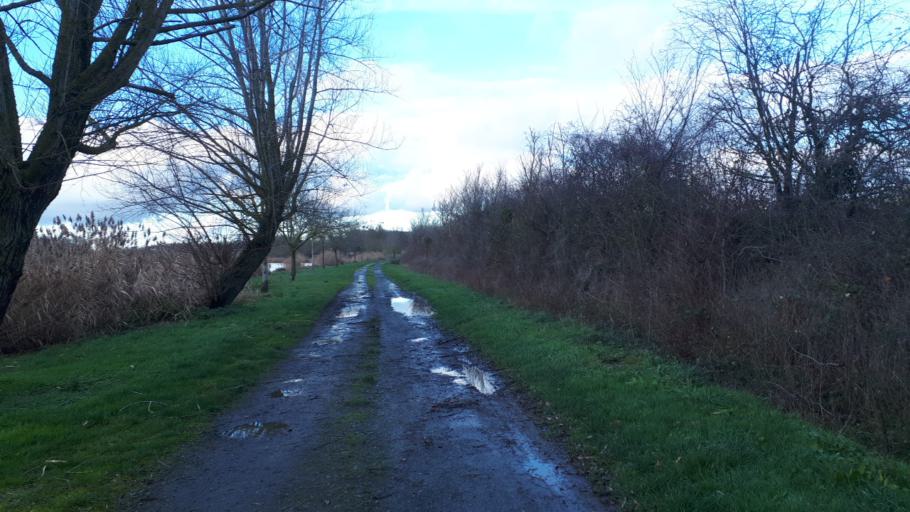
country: FR
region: Poitou-Charentes
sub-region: Departement de la Vienne
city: Pleumartin
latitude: 46.6333
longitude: 0.7663
